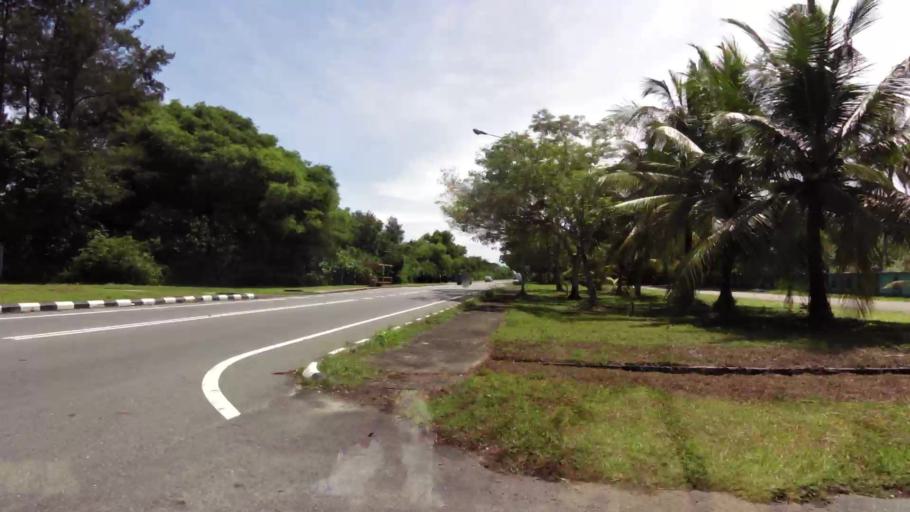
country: BN
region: Belait
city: Kuala Belait
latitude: 4.5927
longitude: 114.2297
